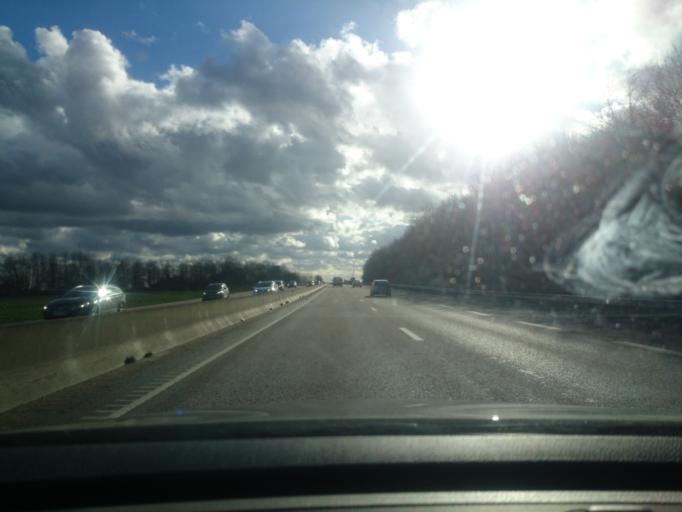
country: SE
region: Skane
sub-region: Lunds Kommun
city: Lund
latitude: 55.6905
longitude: 13.2060
